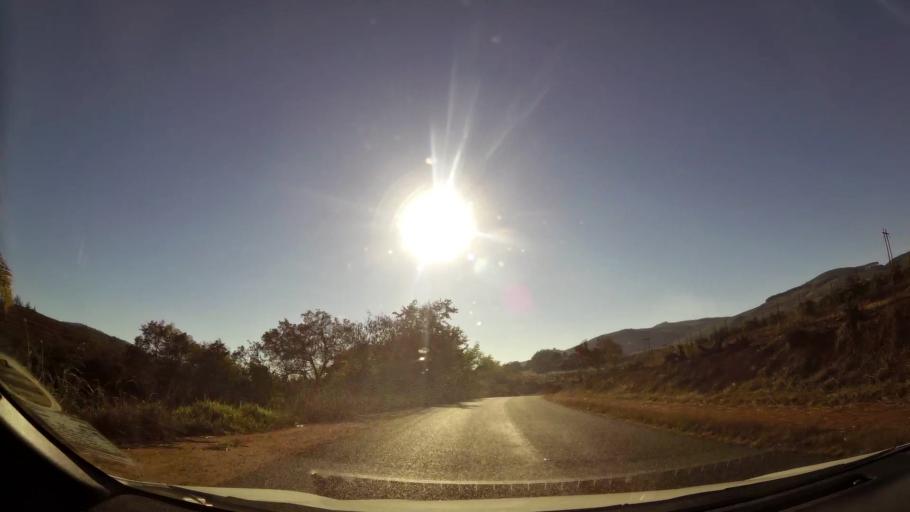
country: ZA
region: Limpopo
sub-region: Mopani District Municipality
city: Tzaneen
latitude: -23.9204
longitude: 30.0494
